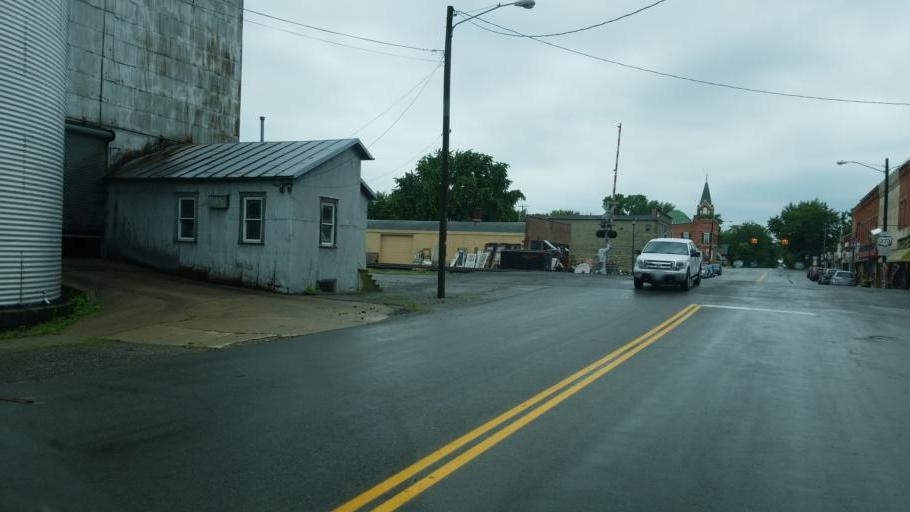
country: US
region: Ohio
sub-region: Hardin County
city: Kenton
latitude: 40.5331
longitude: -83.5203
